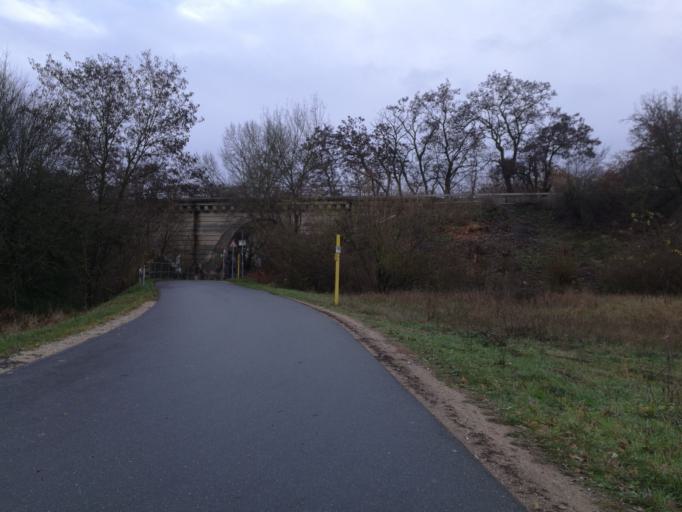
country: DE
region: Bavaria
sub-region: Regierungsbezirk Mittelfranken
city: Wetzendorf
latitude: 49.4655
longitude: 11.0318
